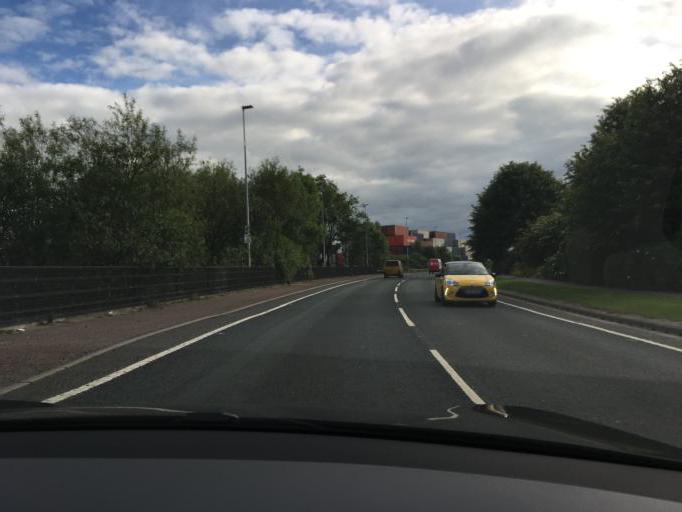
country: GB
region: England
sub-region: City and Borough of Salford
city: Irlam
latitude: 53.4379
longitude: -2.4142
